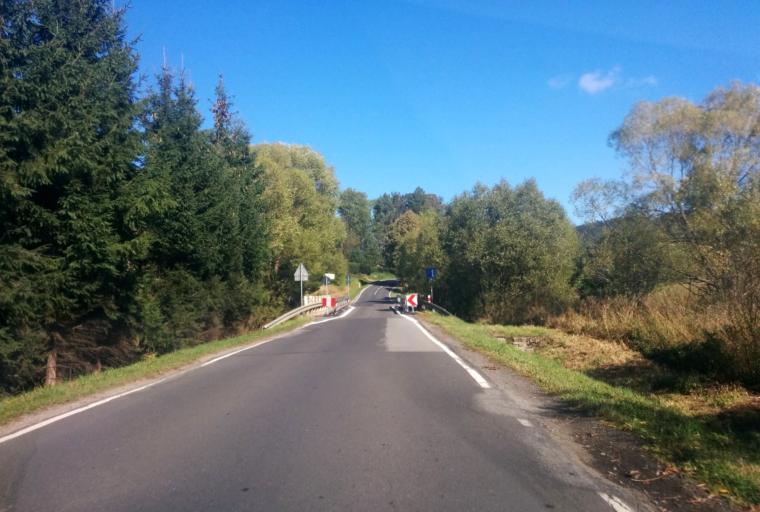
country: PL
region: Subcarpathian Voivodeship
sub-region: Powiat bieszczadzki
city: Lutowiska
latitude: 49.2458
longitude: 22.6935
